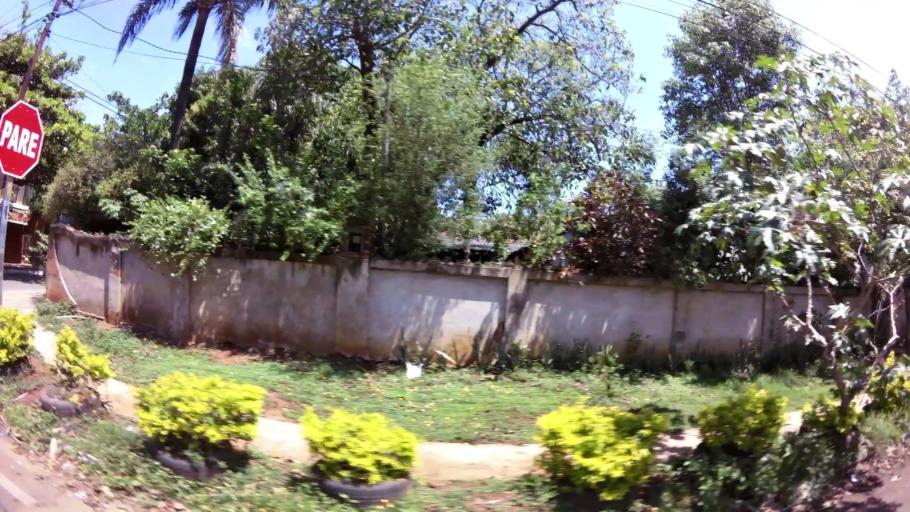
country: PY
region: Central
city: Fernando de la Mora
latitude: -25.3280
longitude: -57.5504
